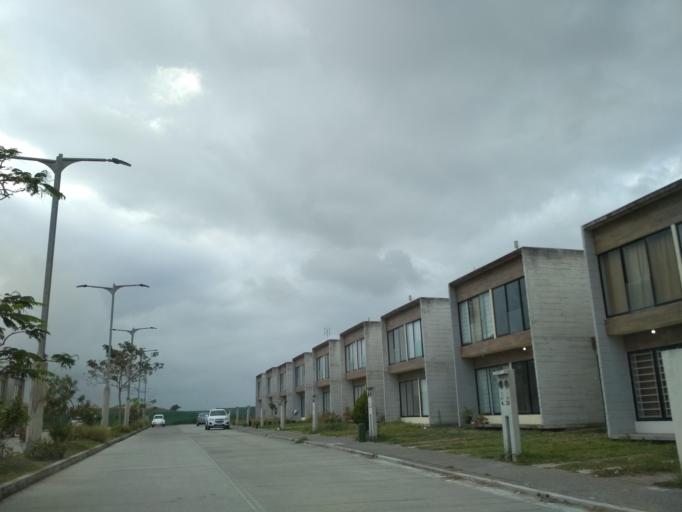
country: MX
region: Veracruz
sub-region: Veracruz
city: Fraccionamiento Geovillas los Pinos
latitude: 19.2193
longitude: -96.2301
